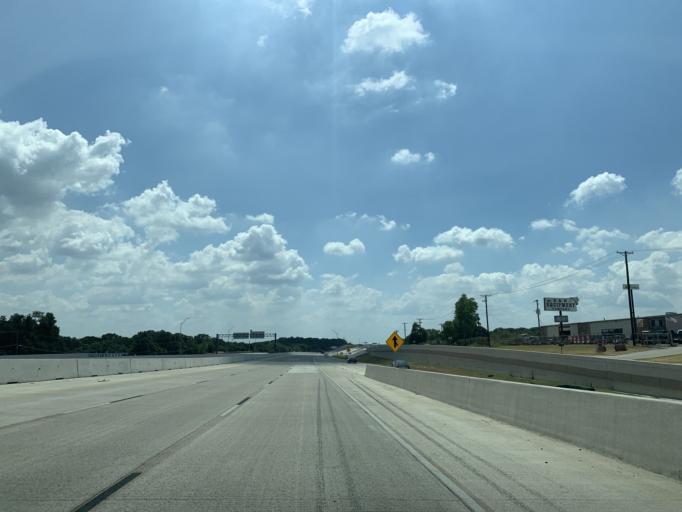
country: US
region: Texas
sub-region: Tarrant County
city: Lakeside
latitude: 32.8533
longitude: -97.5092
